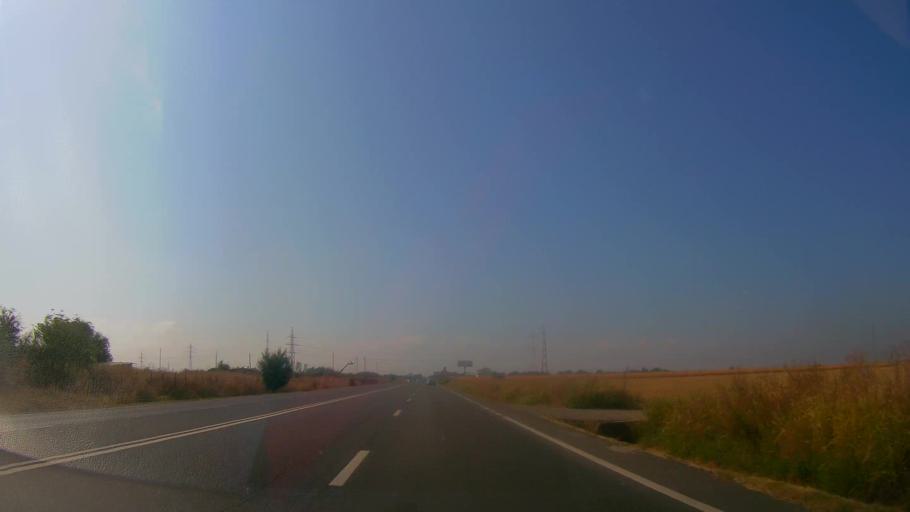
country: RO
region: Giurgiu
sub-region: Comuna Fratesti
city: Remus
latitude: 43.9525
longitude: 25.9813
